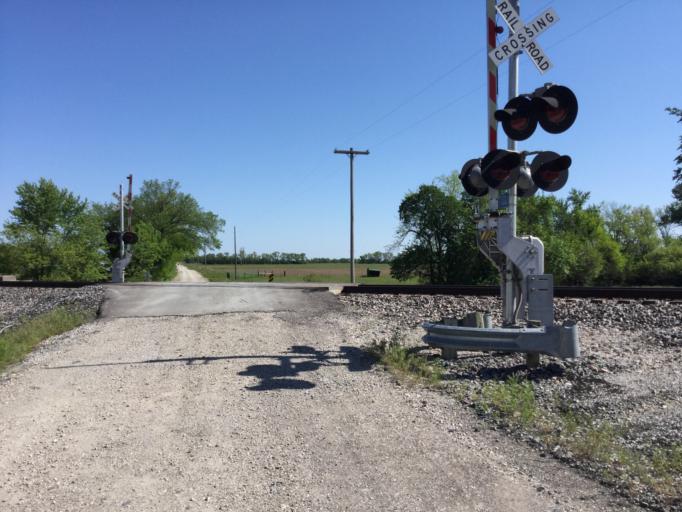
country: US
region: Kansas
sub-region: Labette County
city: Oswego
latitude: 37.2236
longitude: -95.1766
